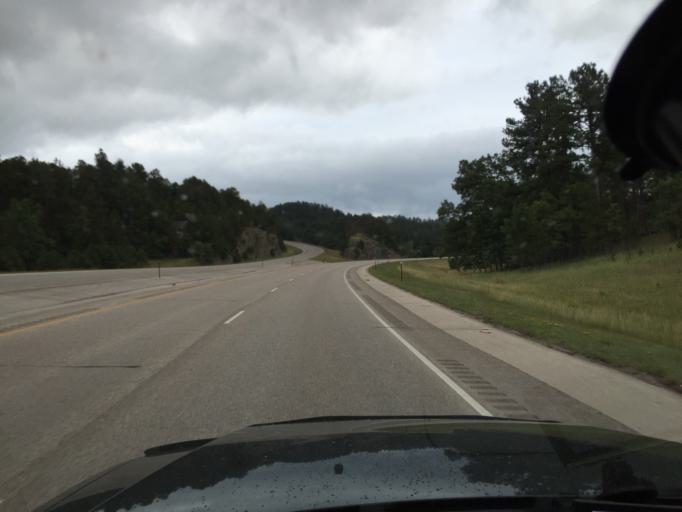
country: US
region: South Dakota
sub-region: Pennington County
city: Colonial Pine Hills
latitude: 43.9432
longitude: -103.3913
